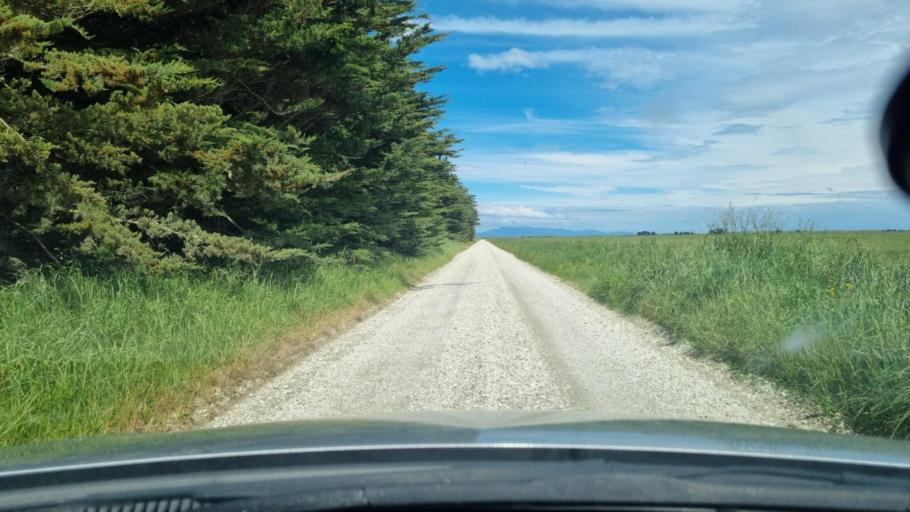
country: NZ
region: Southland
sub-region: Invercargill City
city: Invercargill
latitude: -46.3844
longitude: 168.2661
